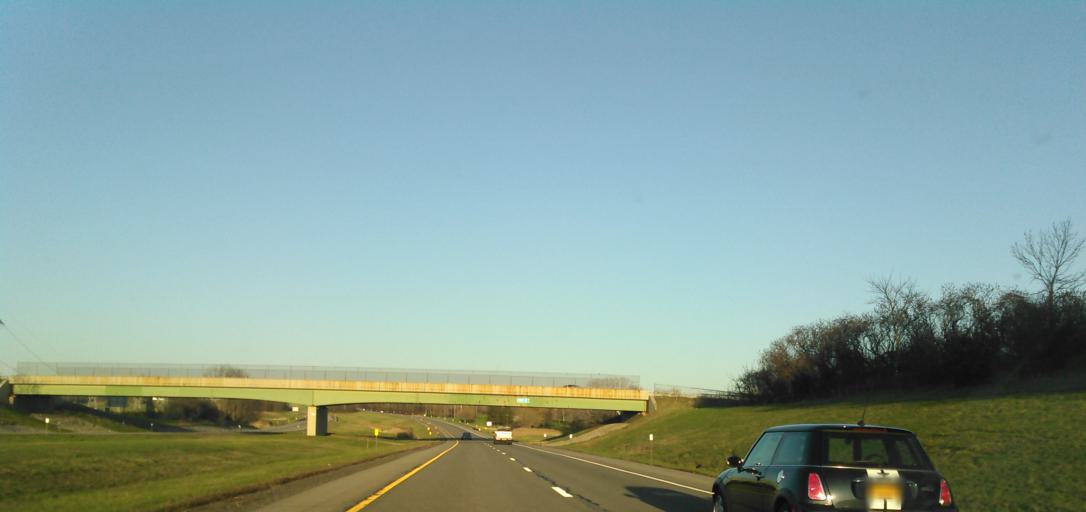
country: US
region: New York
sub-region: Monroe County
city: Honeoye Falls
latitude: 43.0473
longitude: -77.6207
